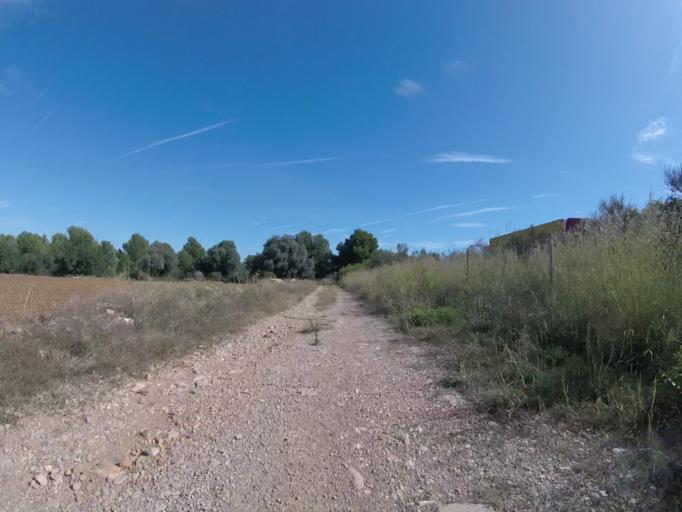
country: ES
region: Valencia
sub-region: Provincia de Castello
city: Peniscola
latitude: 40.3927
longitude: 0.3610
